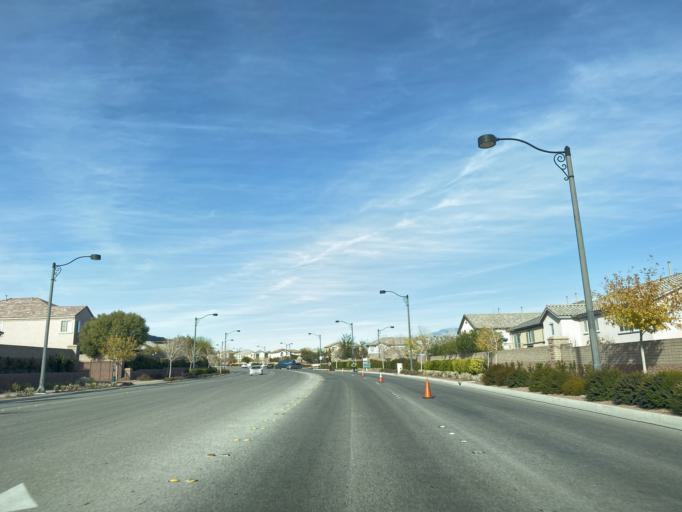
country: US
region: Nevada
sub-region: Clark County
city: Summerlin South
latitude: 36.3001
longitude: -115.3195
